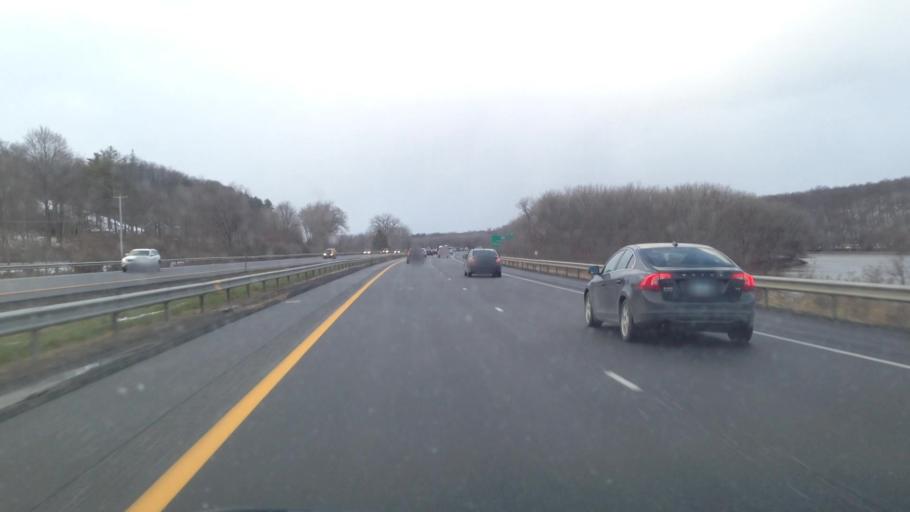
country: US
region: New York
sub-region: Montgomery County
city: Canajoharie
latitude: 42.8977
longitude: -74.5398
